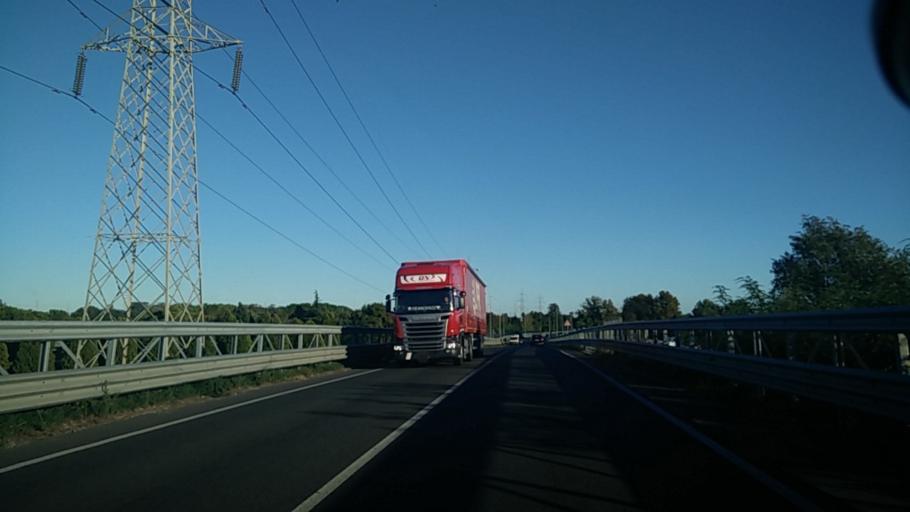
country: IT
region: Veneto
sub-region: Provincia di Venezia
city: Fornase
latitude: 45.4624
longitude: 12.1793
